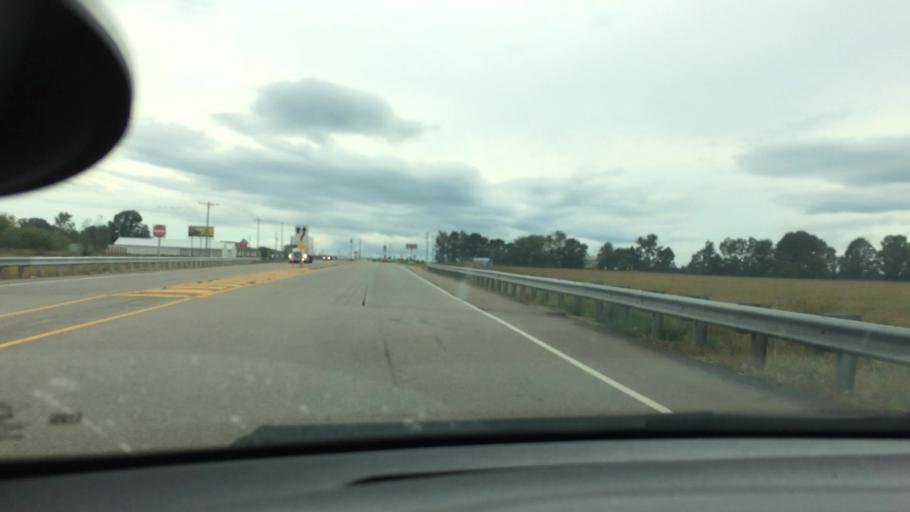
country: US
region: Wisconsin
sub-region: Trempealeau County
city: Osseo
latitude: 44.5826
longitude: -91.1929
